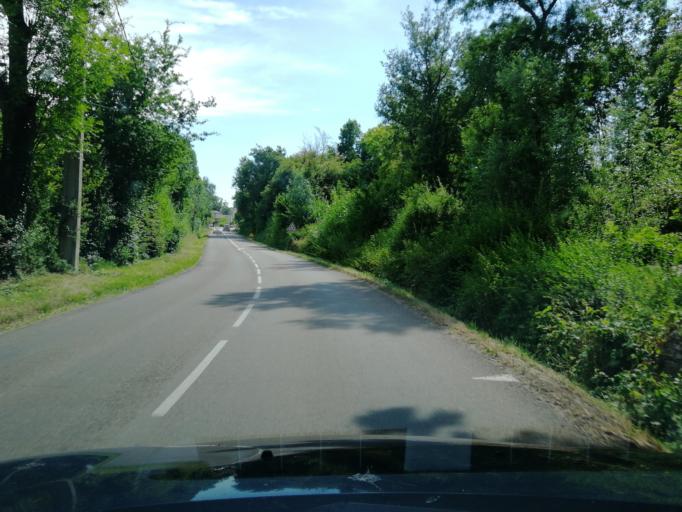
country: FR
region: Rhone-Alpes
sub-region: Departement du Rhone
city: Mornant
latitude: 45.6280
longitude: 4.6705
